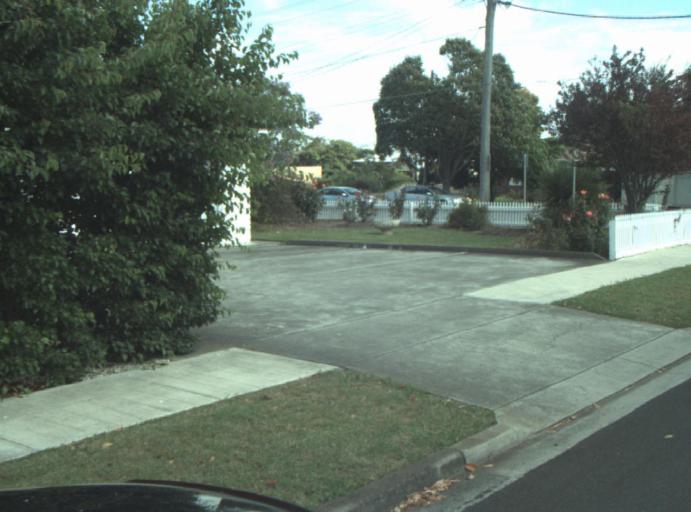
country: AU
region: Victoria
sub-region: Greater Geelong
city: Breakwater
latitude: -38.1703
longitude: 144.3374
